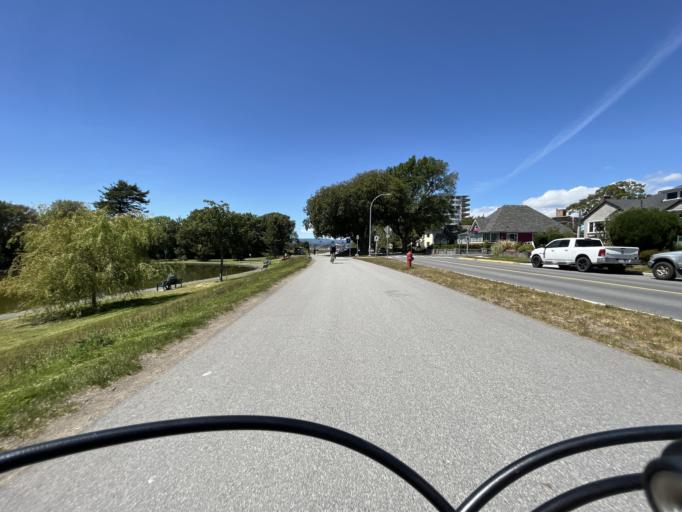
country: CA
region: British Columbia
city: Victoria
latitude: 48.4100
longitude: -123.3735
